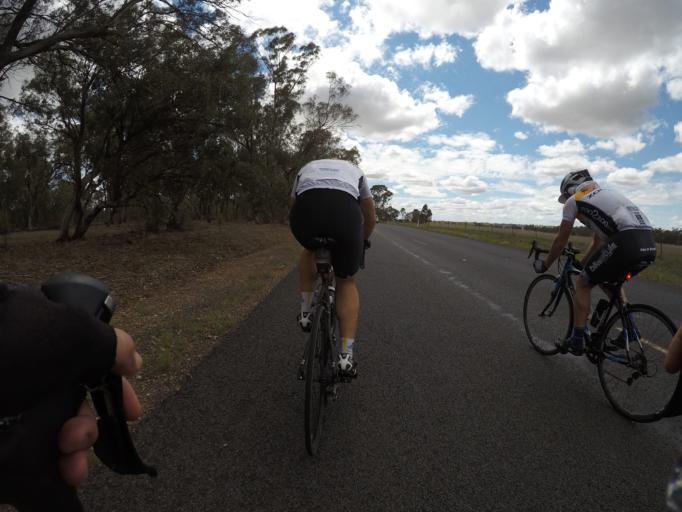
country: AU
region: New South Wales
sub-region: Dubbo Municipality
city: Dubbo
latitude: -32.4685
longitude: 148.5685
